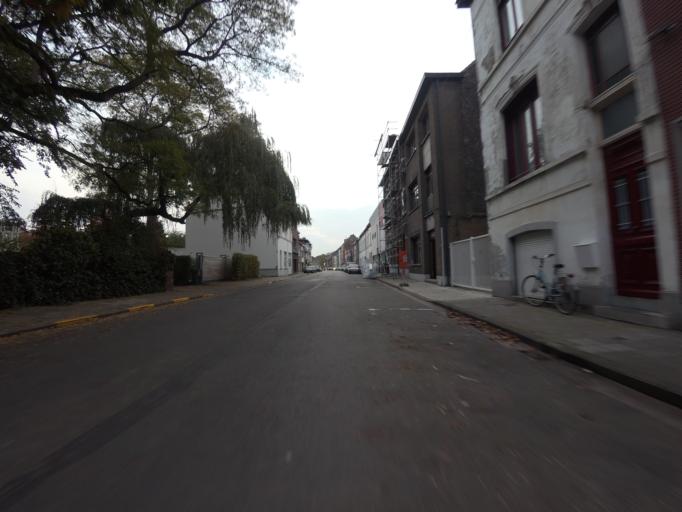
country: BE
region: Flanders
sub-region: Provincie Oost-Vlaanderen
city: Ledeberg
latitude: 51.0667
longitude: 3.7490
